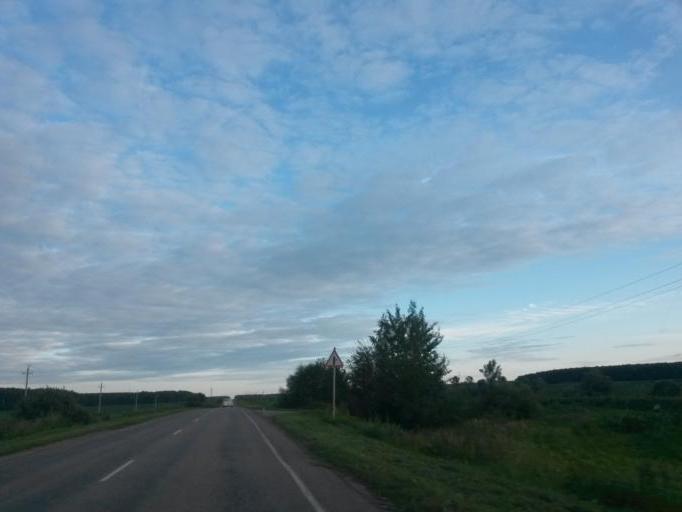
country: RU
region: Moskovskaya
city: Barybino
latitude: 55.2093
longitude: 37.7877
